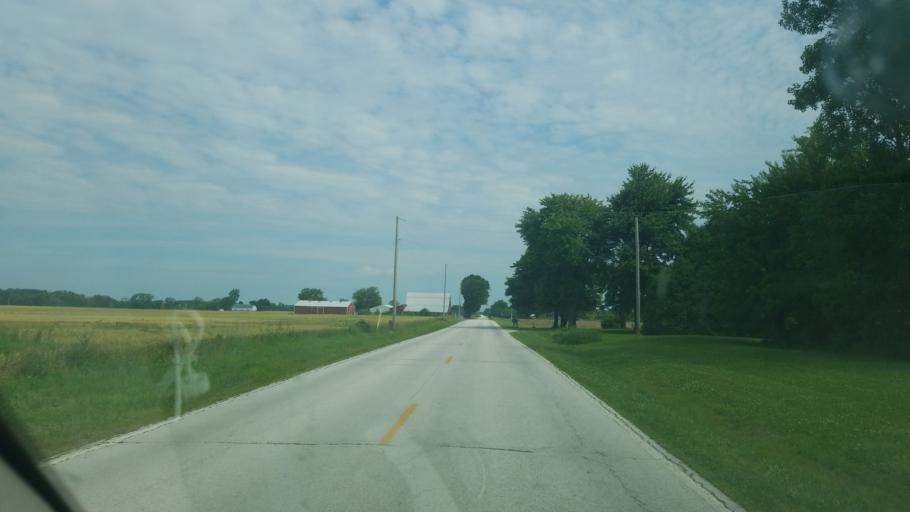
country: US
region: Ohio
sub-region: Seneca County
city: Fostoria
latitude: 41.0853
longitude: -83.4783
